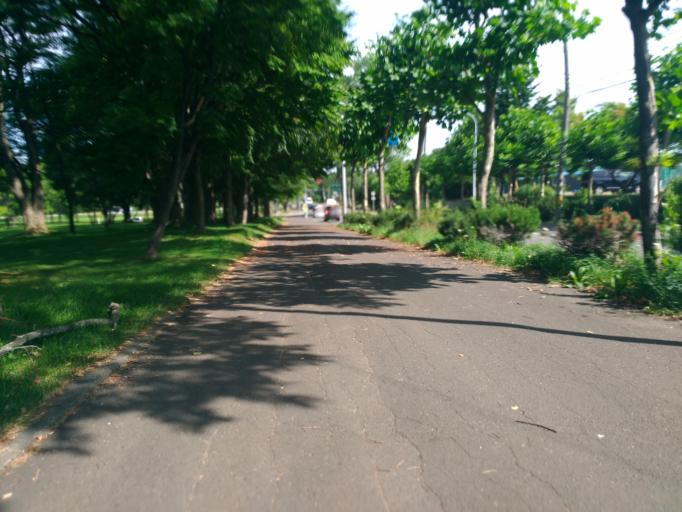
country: JP
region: Hokkaido
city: Ebetsu
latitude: 43.0708
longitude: 141.5015
